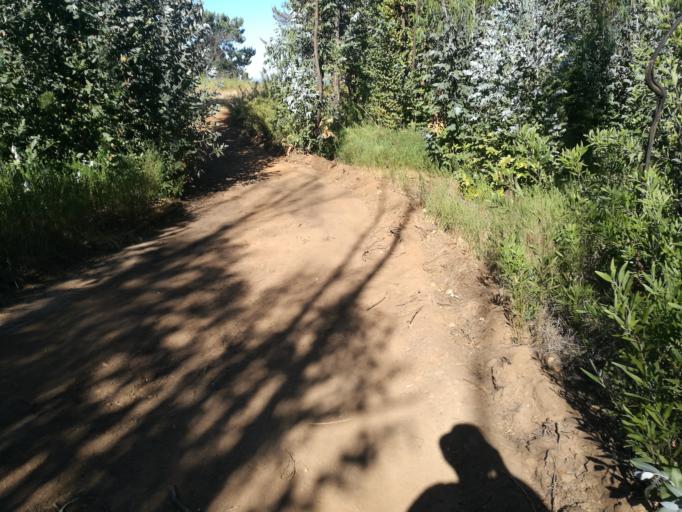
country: CL
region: Valparaiso
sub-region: Provincia de Valparaiso
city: Valparaiso
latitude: -33.0703
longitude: -71.6506
